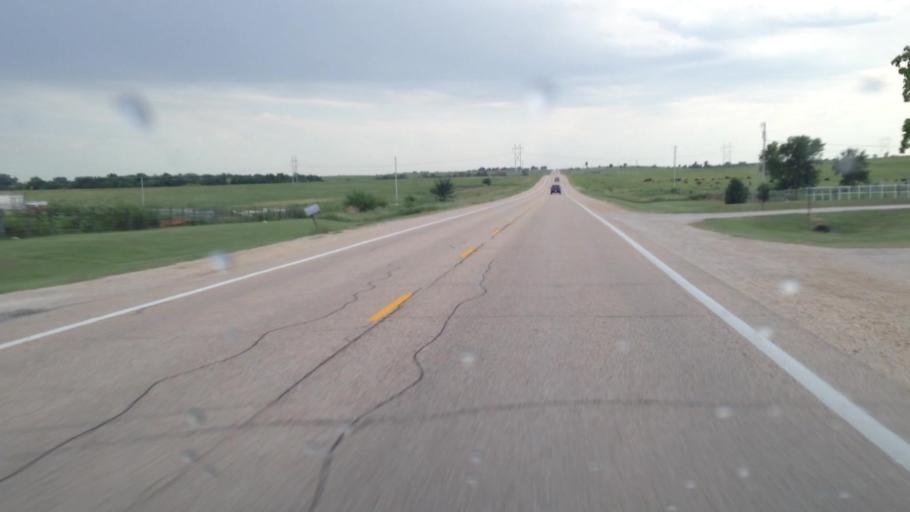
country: US
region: Kansas
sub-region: Coffey County
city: Burlington
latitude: 38.1648
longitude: -95.7390
